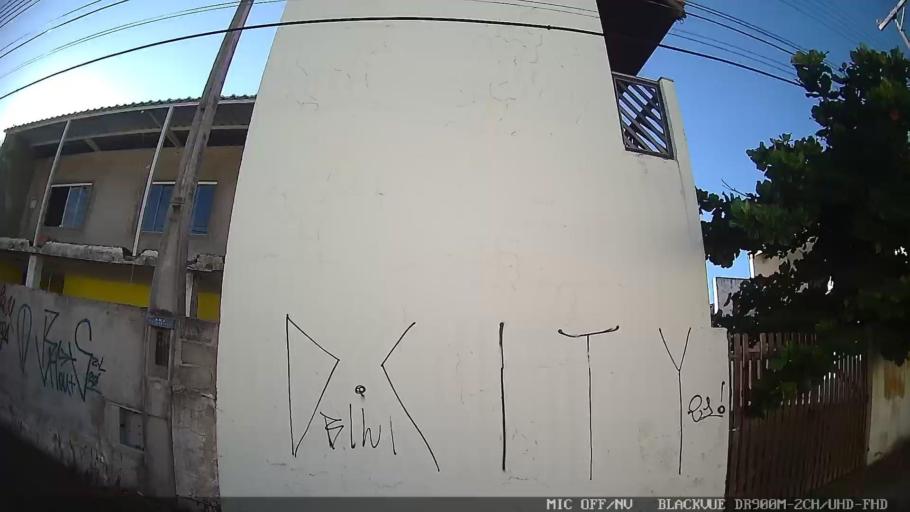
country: BR
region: Sao Paulo
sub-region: Peruibe
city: Peruibe
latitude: -24.3257
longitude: -46.9975
